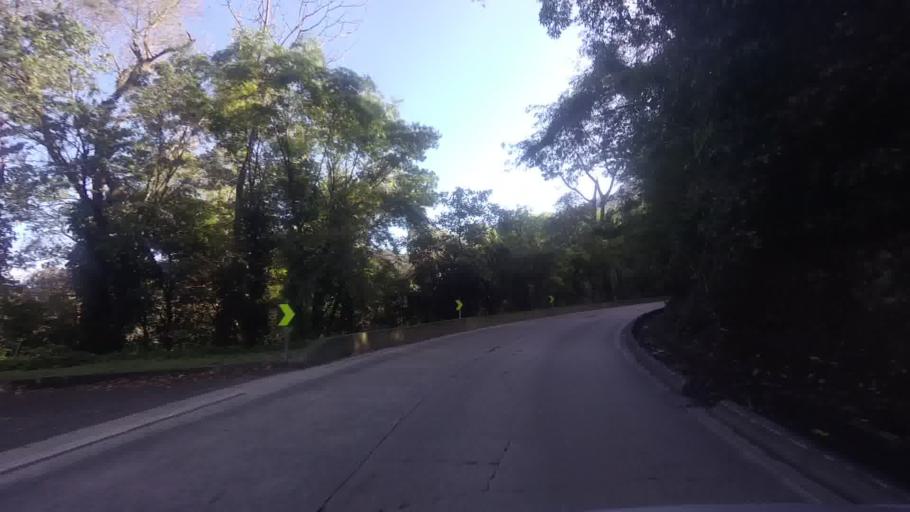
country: BR
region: Rio de Janeiro
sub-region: Petropolis
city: Petropolis
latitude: -22.5626
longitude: -43.2365
